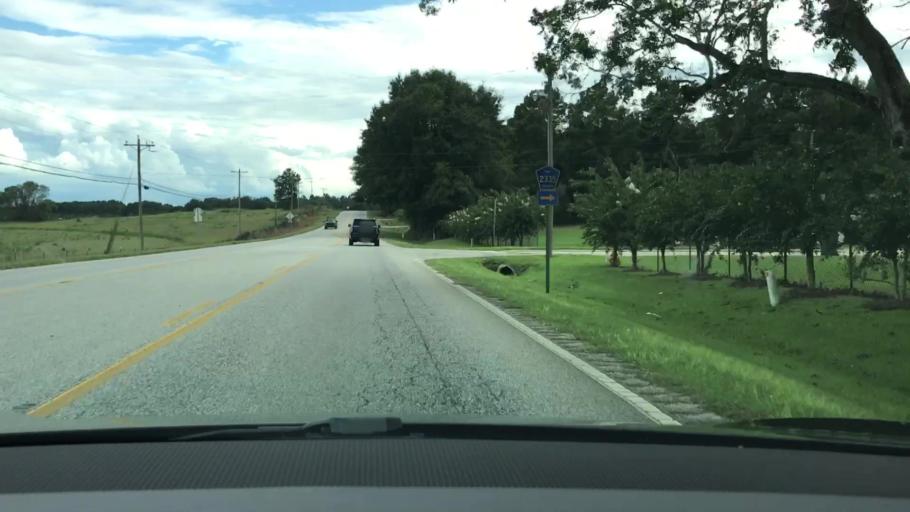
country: US
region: Alabama
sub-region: Pike County
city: Troy
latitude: 31.7051
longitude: -85.9589
